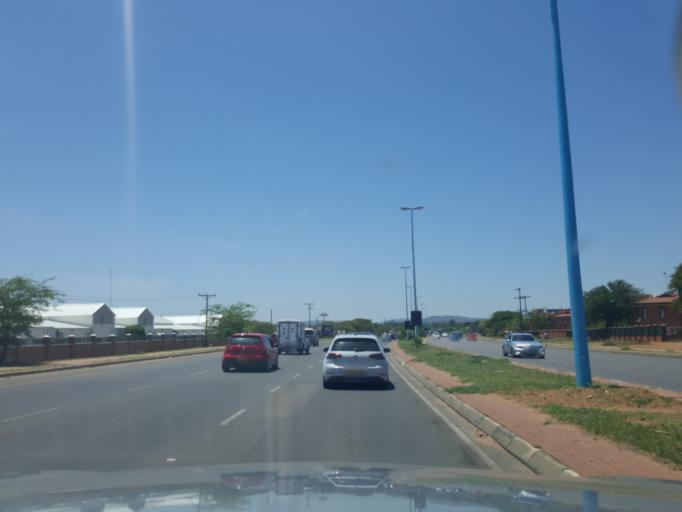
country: BW
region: Kweneng
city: Mogoditshane
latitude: -24.6368
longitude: 25.8786
